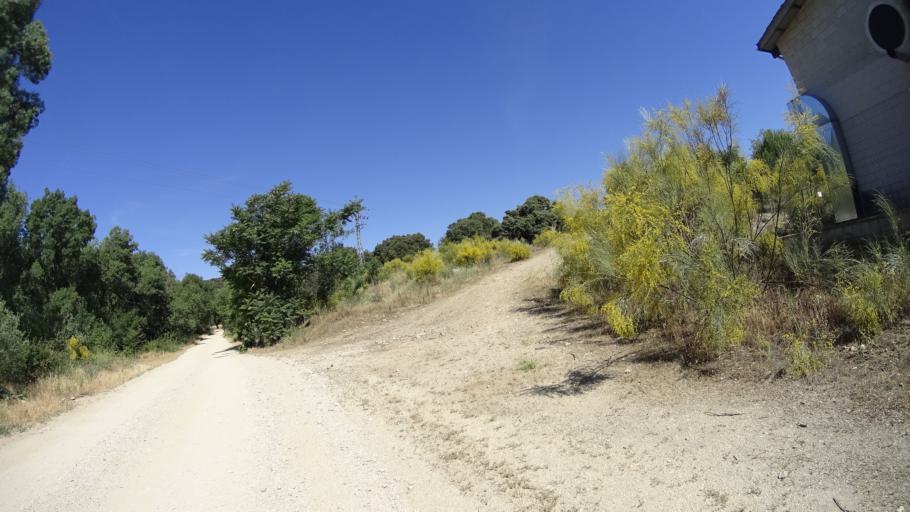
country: ES
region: Madrid
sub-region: Provincia de Madrid
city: Galapagar
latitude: 40.5864
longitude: -3.9668
